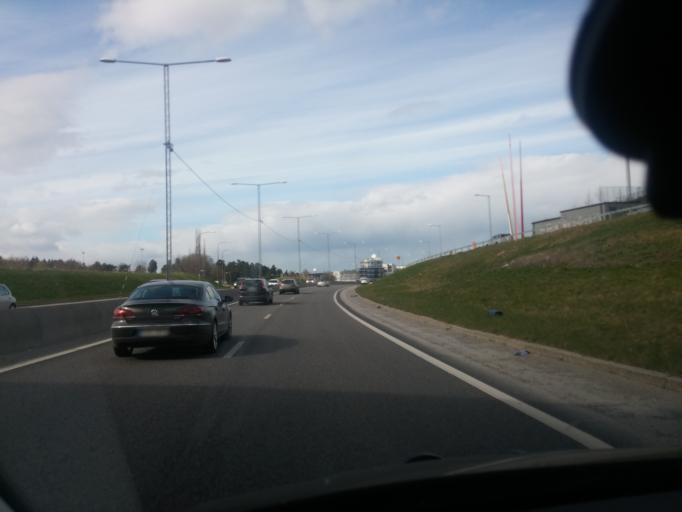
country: SE
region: Stockholm
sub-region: Stockholms Kommun
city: Bromma
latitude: 59.3612
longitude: 17.9435
